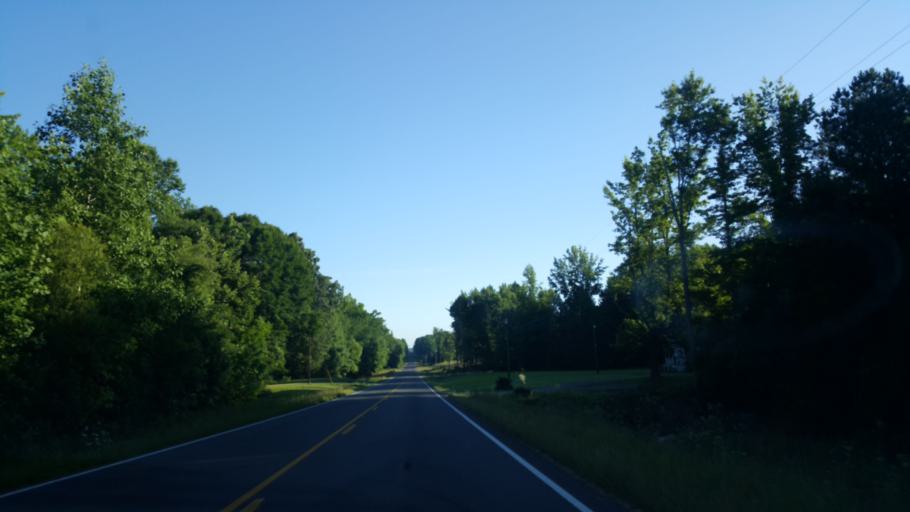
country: US
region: Tennessee
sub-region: Henderson County
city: Lexington
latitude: 35.5408
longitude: -88.3834
